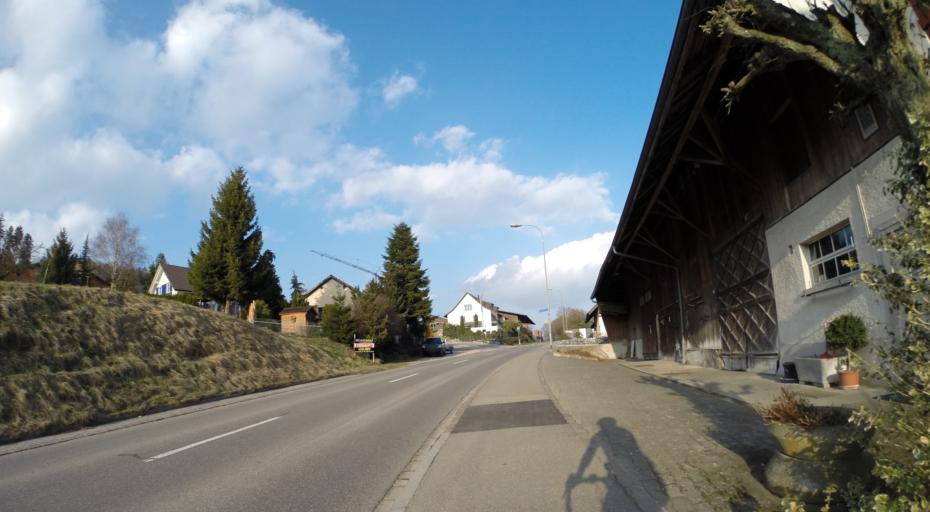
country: CH
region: Thurgau
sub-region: Frauenfeld District
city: Huttwilen
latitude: 47.6080
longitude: 8.9119
